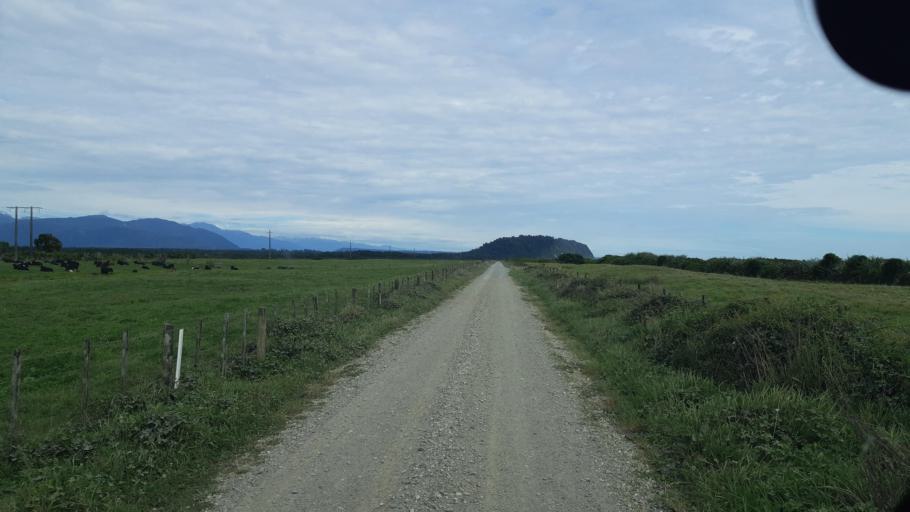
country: NZ
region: West Coast
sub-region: Westland District
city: Hokitika
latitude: -42.9145
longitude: 170.7454
